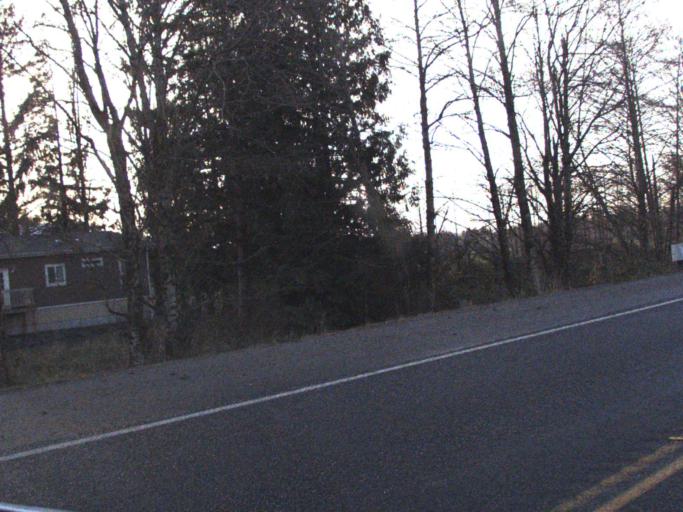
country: US
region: Washington
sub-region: Skagit County
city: Sedro-Woolley
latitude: 48.5234
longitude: -121.9634
